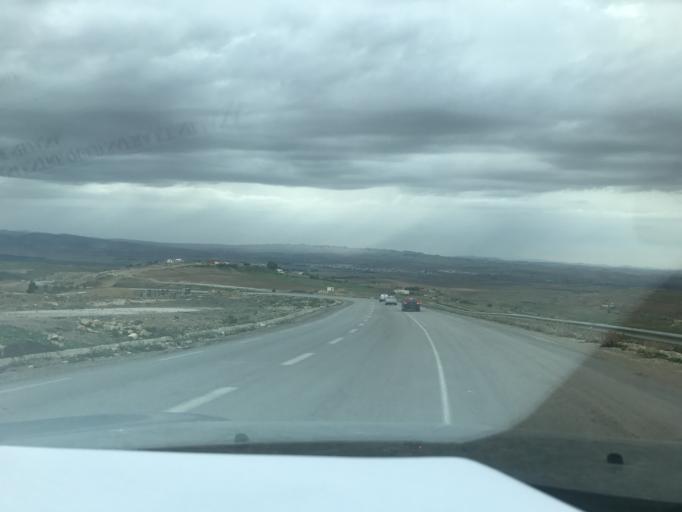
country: TN
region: Silyanah
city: Siliana
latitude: 36.0924
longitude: 9.4717
